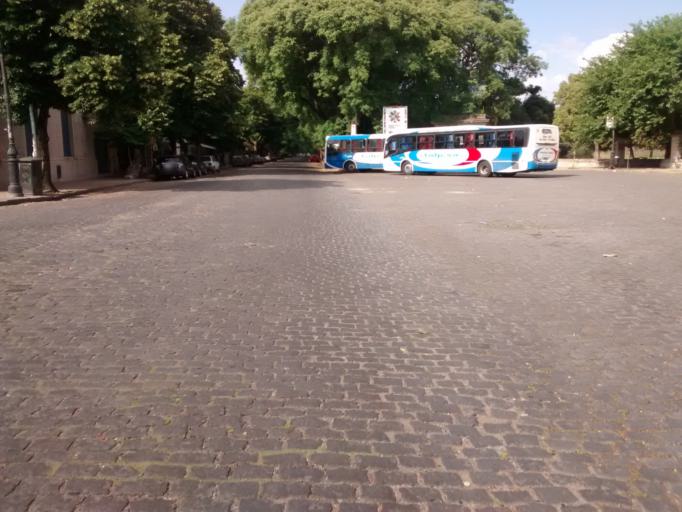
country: AR
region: Buenos Aires
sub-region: Partido de La Plata
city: La Plata
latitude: -34.9397
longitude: -57.9394
